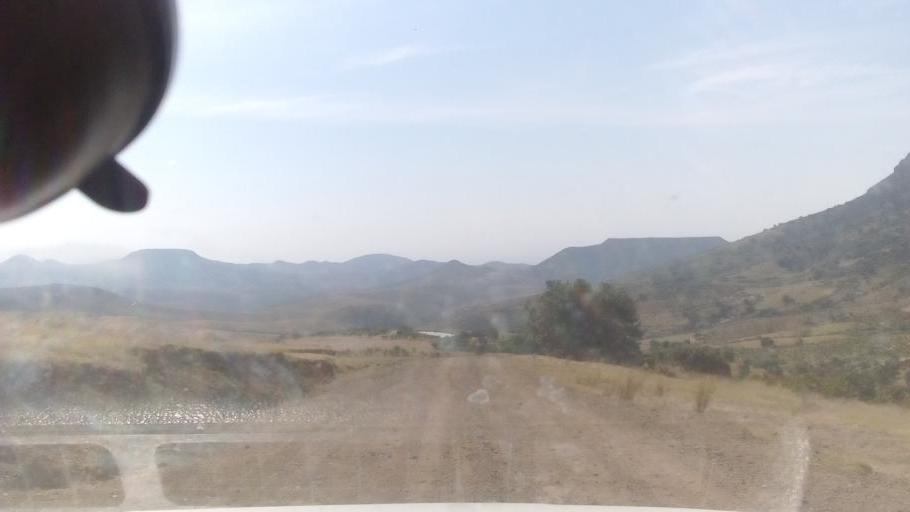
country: MX
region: Guanajuato
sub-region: Leon
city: Lucio Blanco (Los Gavilanes)
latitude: 21.2045
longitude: -101.5003
